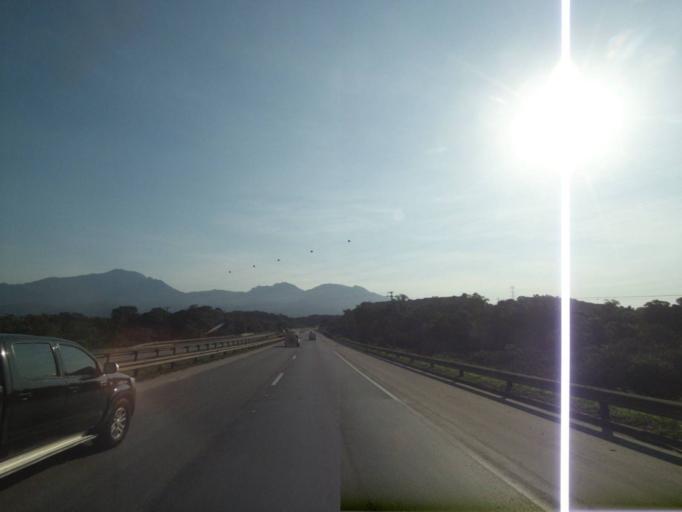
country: BR
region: Parana
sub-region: Paranagua
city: Paranagua
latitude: -25.5663
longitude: -48.6072
